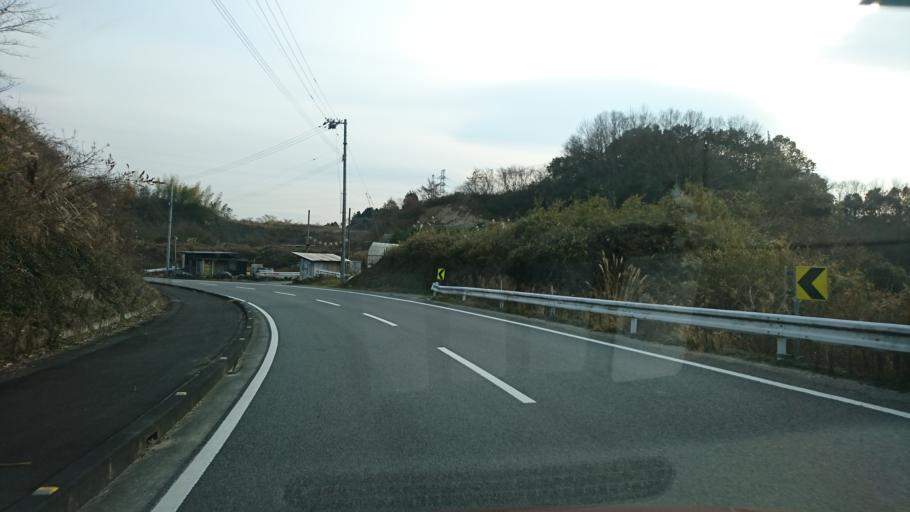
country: JP
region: Ehime
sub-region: Shikoku-chuo Shi
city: Matsuyama
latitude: 33.8889
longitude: 132.8018
